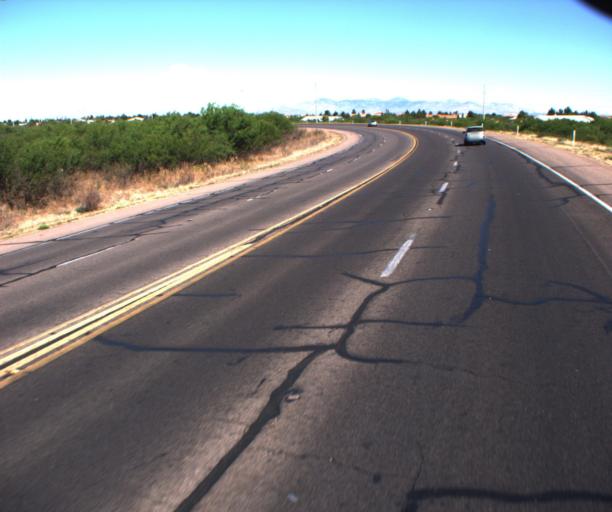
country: US
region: Arizona
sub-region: Cochise County
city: Sierra Vista
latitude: 31.5668
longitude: -110.2575
